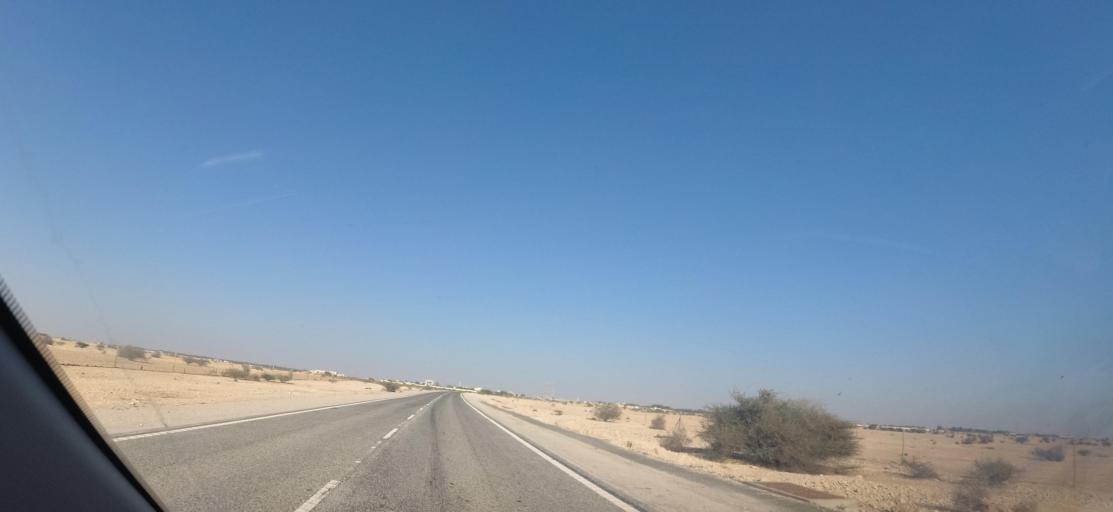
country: QA
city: Al Ghuwayriyah
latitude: 25.8180
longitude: 51.2348
